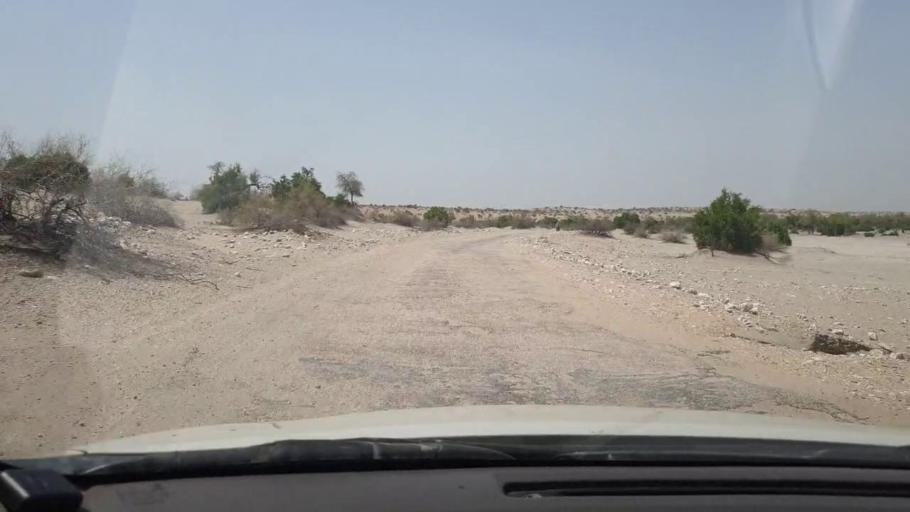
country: PK
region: Sindh
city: Rohri
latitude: 27.3047
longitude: 69.2814
